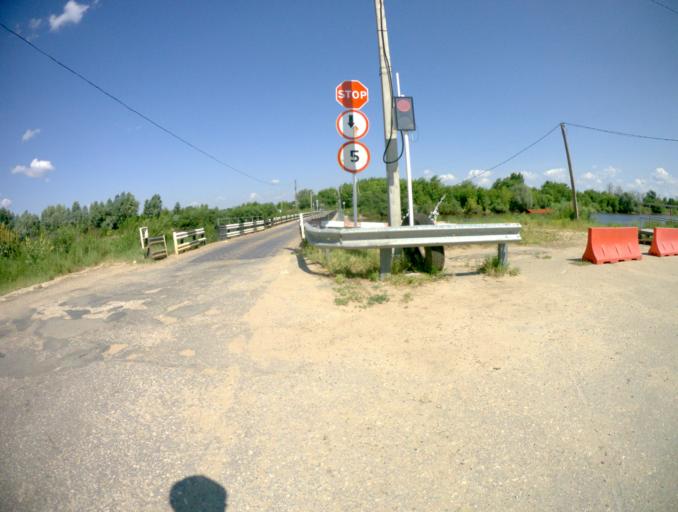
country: RU
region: Vladimir
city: Vyazniki
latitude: 56.2546
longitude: 42.1789
